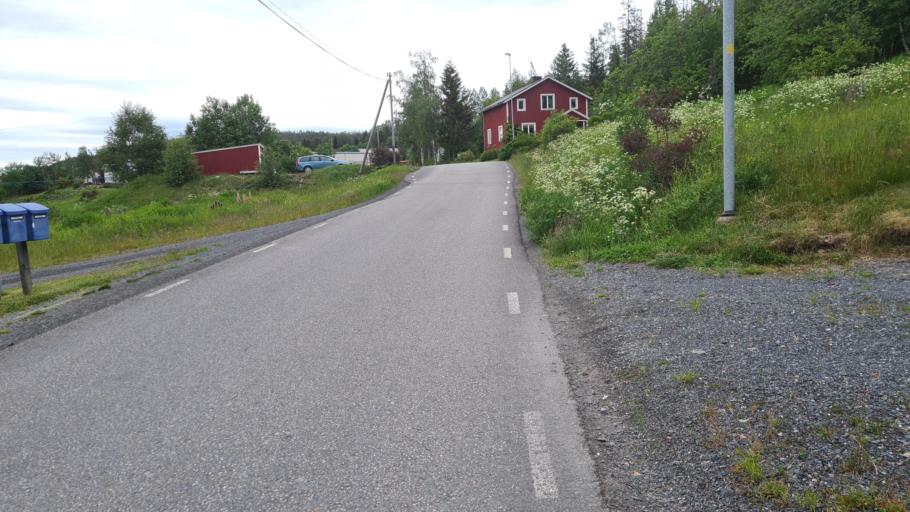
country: SE
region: Vaesternorrland
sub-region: Kramfors Kommun
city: Nordingra
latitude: 62.9804
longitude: 18.4301
